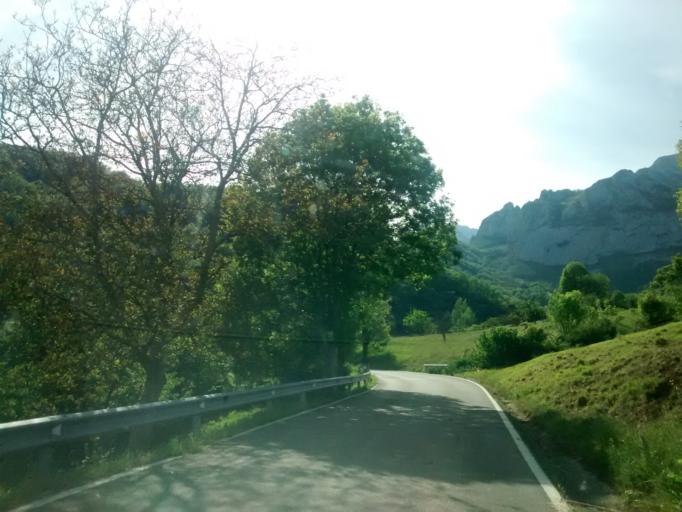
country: ES
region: Cantabria
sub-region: Provincia de Cantabria
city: Potes
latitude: 43.1910
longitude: -4.6327
